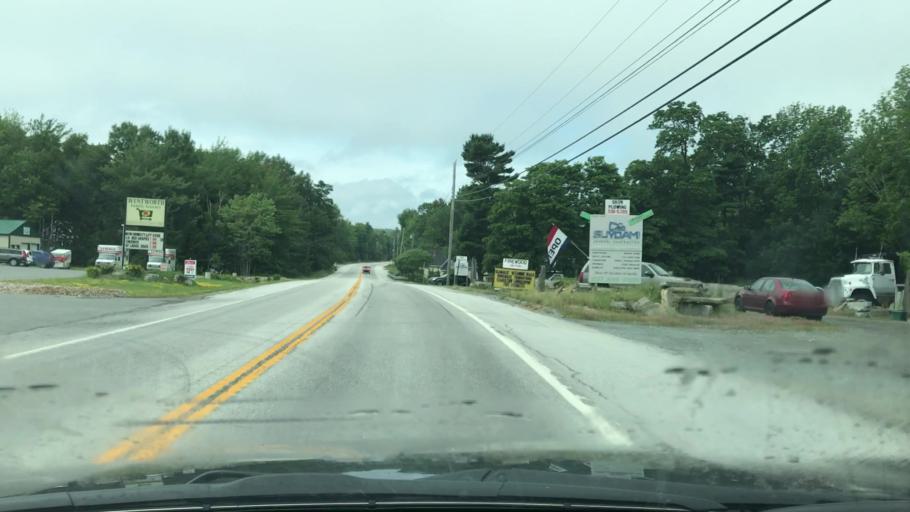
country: US
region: Maine
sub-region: Waldo County
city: Northport
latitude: 44.3364
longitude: -68.9591
